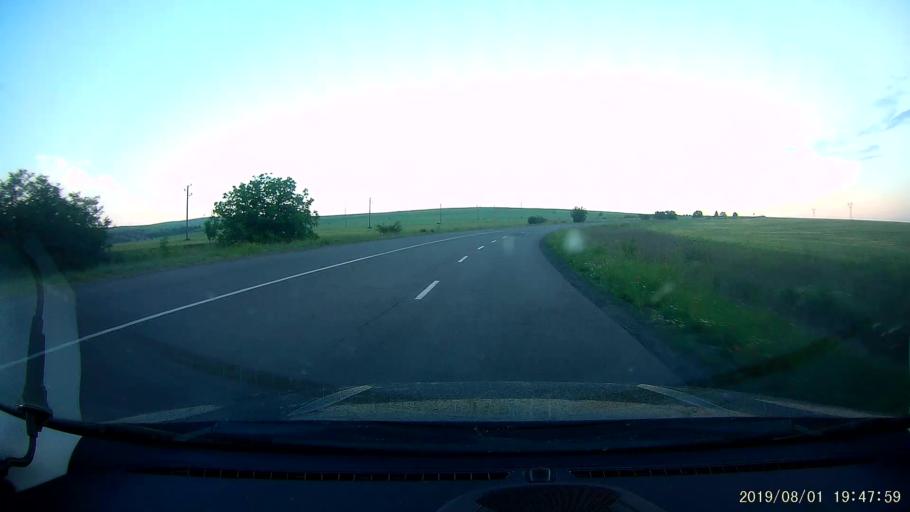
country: BG
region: Burgas
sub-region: Obshtina Karnobat
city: Karnobat
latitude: 42.6431
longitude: 26.9574
